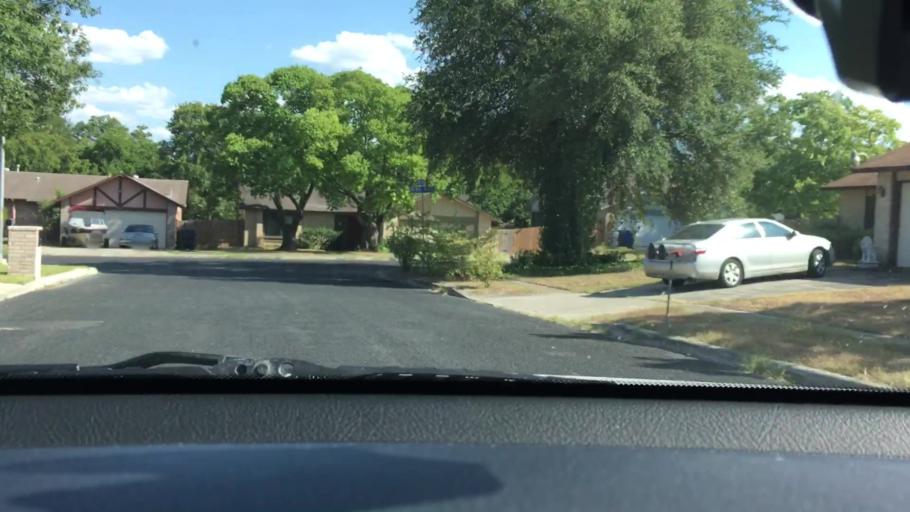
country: US
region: Texas
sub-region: Bexar County
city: Live Oak
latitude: 29.5915
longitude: -98.3709
